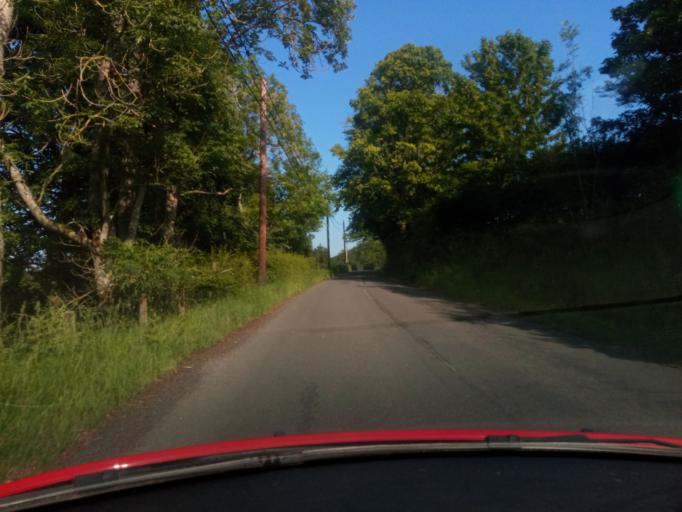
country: GB
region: Scotland
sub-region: The Scottish Borders
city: Selkirk
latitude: 55.5108
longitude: -2.9624
